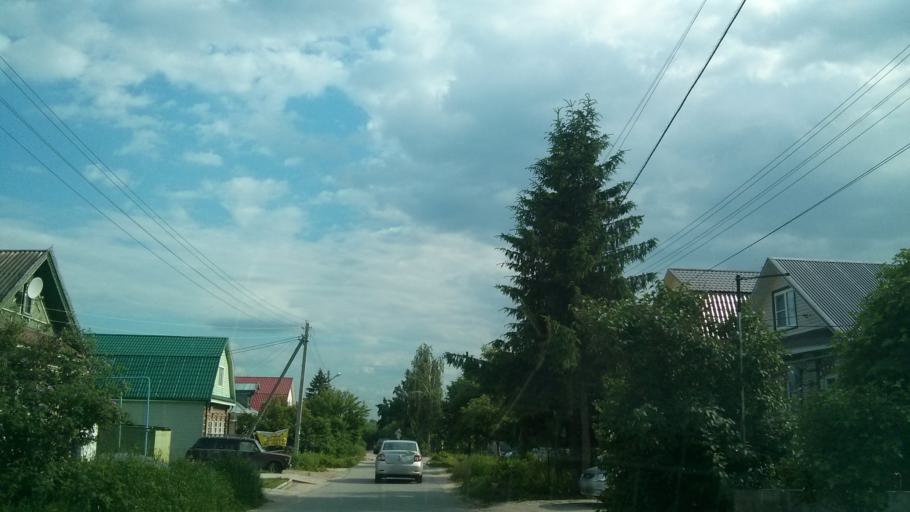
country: RU
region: Nizjnij Novgorod
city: Afonino
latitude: 56.2856
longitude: 44.1004
